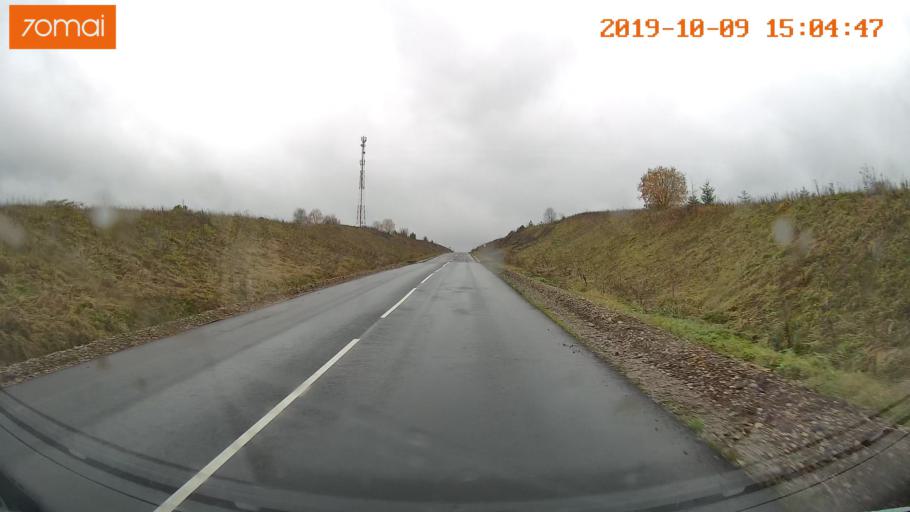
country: RU
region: Kostroma
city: Chistyye Bory
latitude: 58.2540
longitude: 41.6641
